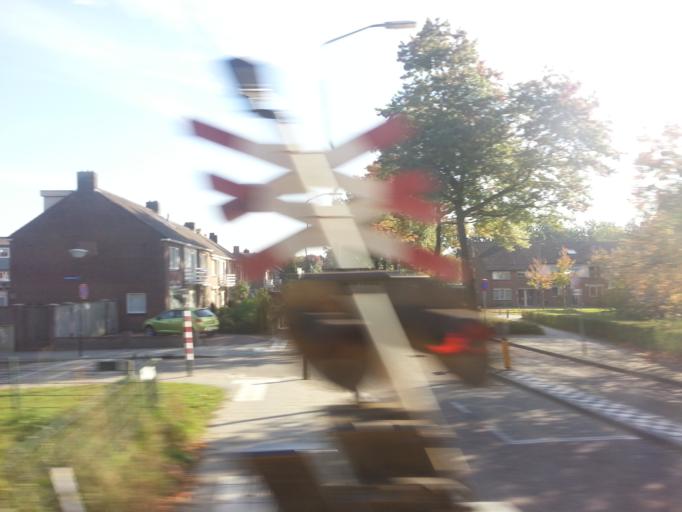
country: NL
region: North Brabant
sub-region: Gemeente Vught
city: Vught
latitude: 51.6481
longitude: 5.2931
